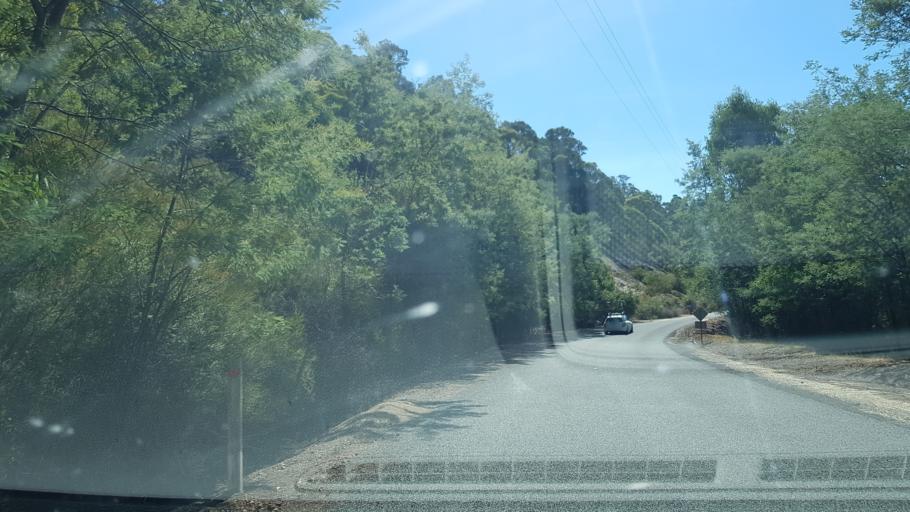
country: AU
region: Victoria
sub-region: Mansfield
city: Mansfield
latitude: -36.9053
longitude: 146.3913
